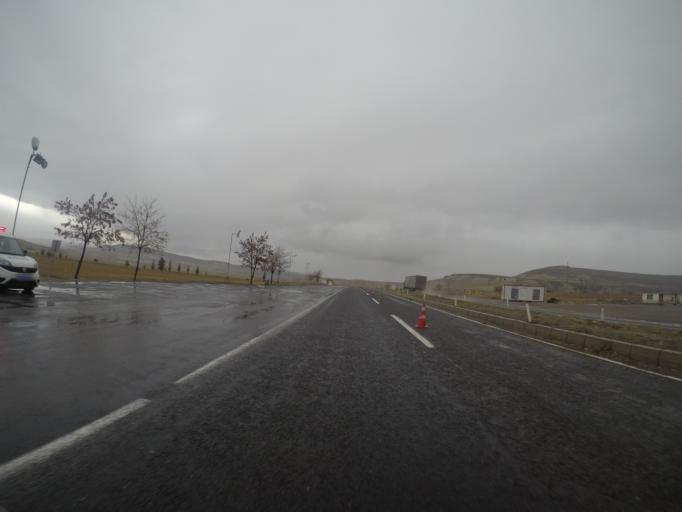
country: TR
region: Nevsehir
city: Urgub
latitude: 38.7324
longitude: 34.9706
